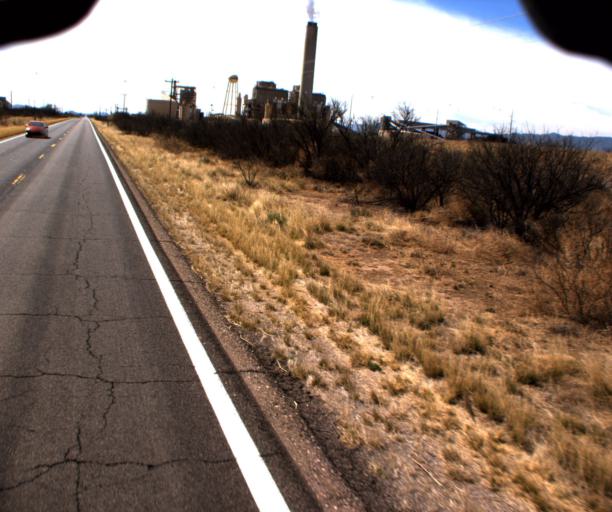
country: US
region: Arizona
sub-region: Cochise County
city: Willcox
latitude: 32.0681
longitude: -109.8952
